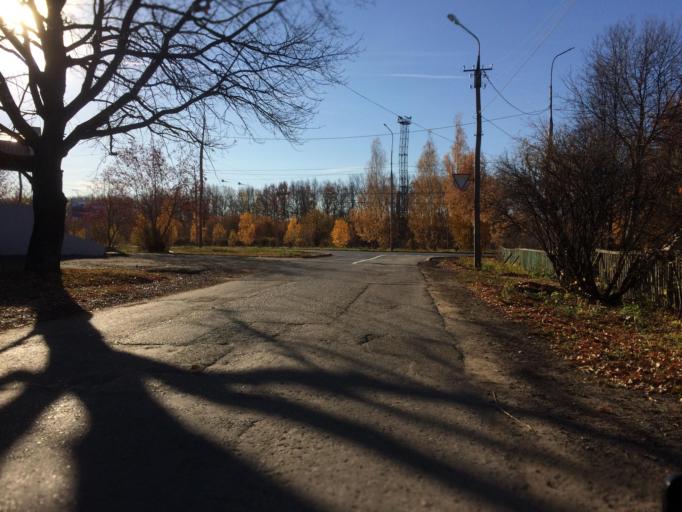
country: RU
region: Mariy-El
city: Medvedevo
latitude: 56.6292
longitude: 47.8095
